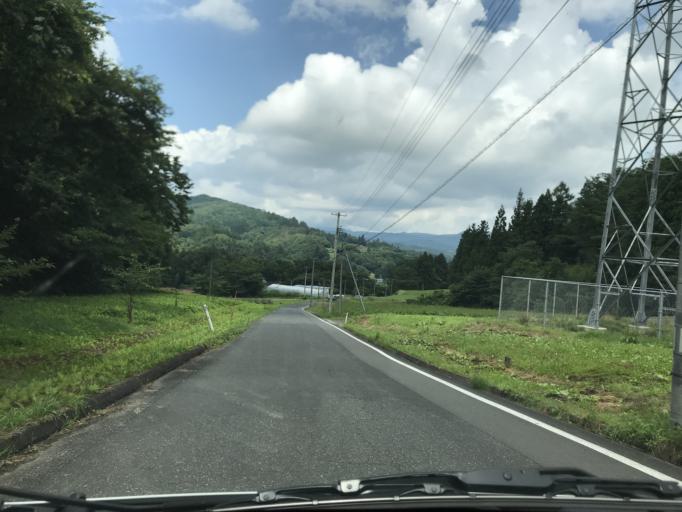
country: JP
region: Iwate
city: Mizusawa
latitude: 39.0375
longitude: 141.3514
